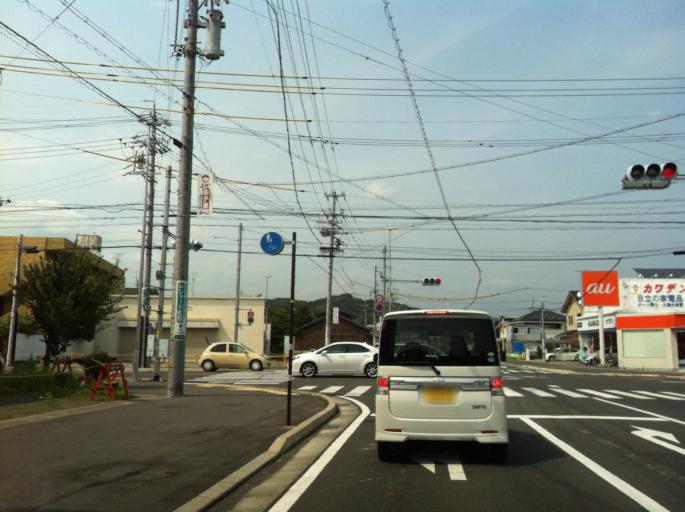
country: JP
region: Shizuoka
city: Shimada
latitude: 34.8348
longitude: 138.1783
